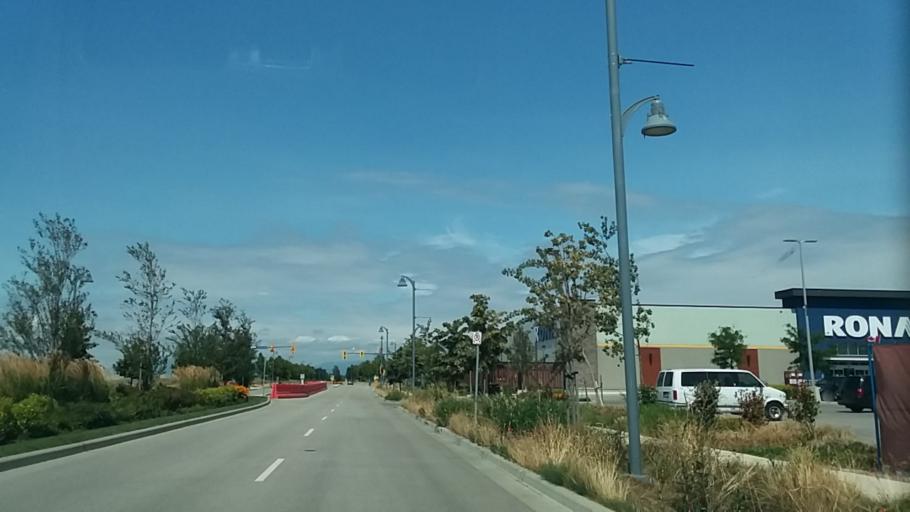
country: CA
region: British Columbia
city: Ladner
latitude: 49.0418
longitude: -123.0902
